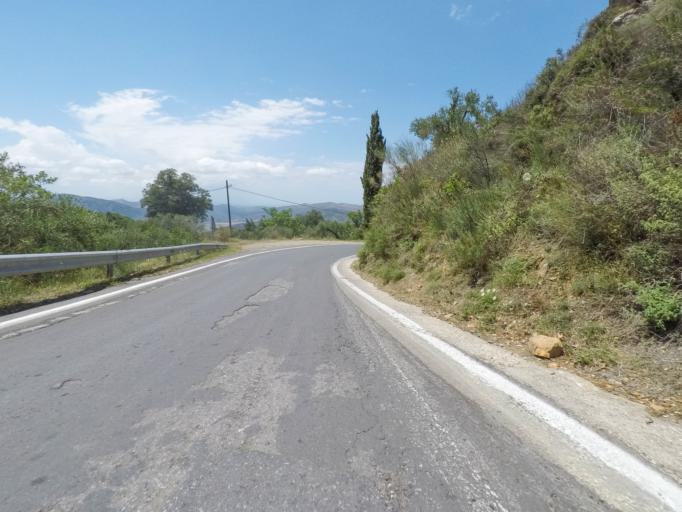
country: GR
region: Crete
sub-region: Nomos Irakleiou
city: Mokhos
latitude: 35.2217
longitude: 25.4627
